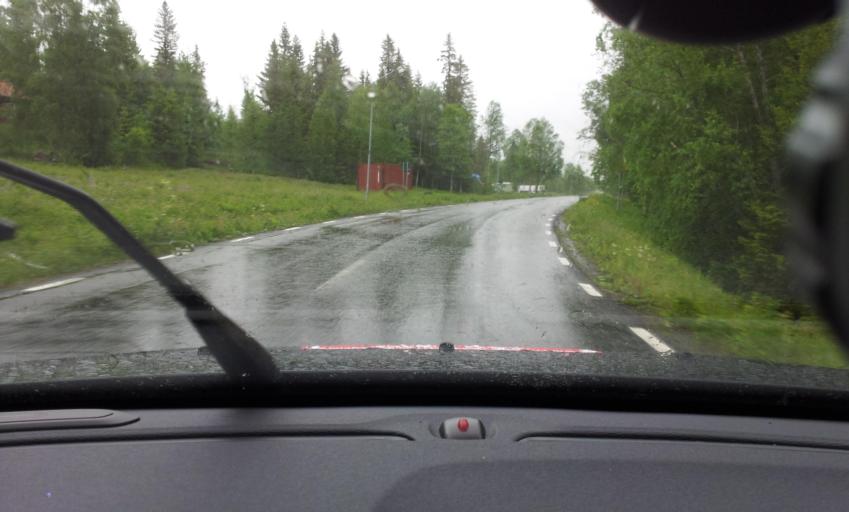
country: SE
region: Jaemtland
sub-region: Are Kommun
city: Are
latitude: 63.3158
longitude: 13.1070
